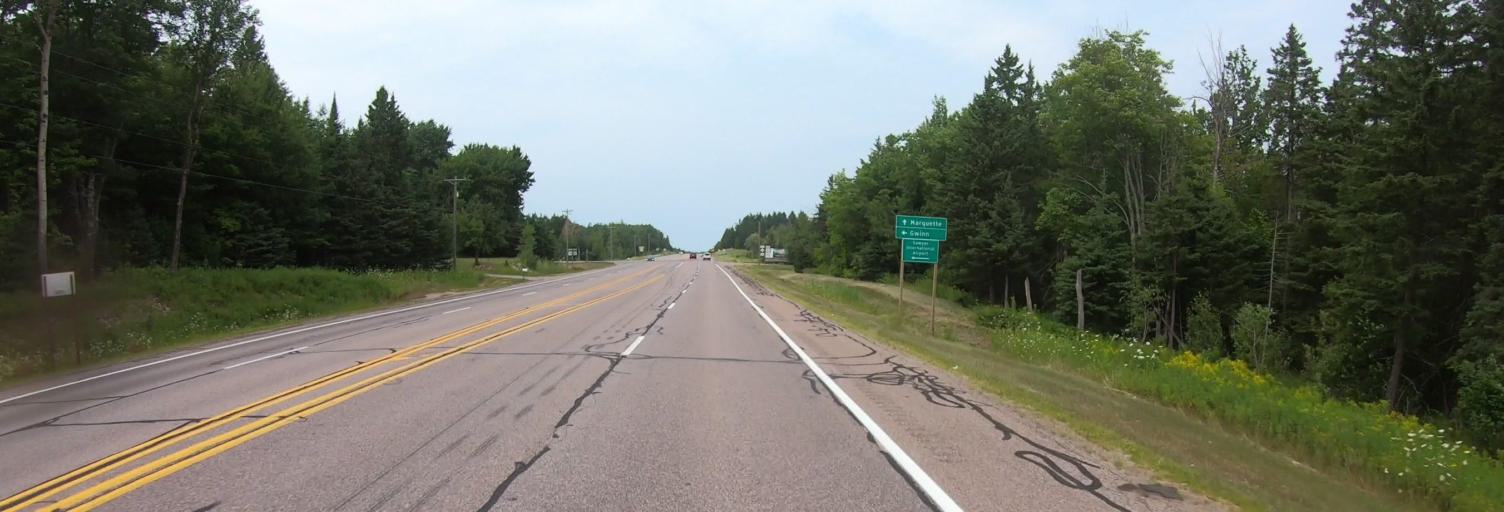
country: US
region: Michigan
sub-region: Marquette County
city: K. I. Sawyer Air Force Base
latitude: 46.3610
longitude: -87.2243
